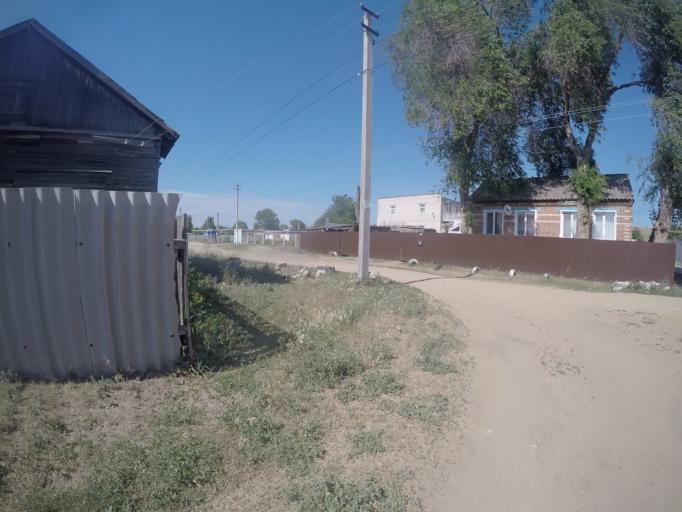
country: RU
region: Saratov
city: Privolzhskiy
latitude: 51.1799
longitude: 45.9180
